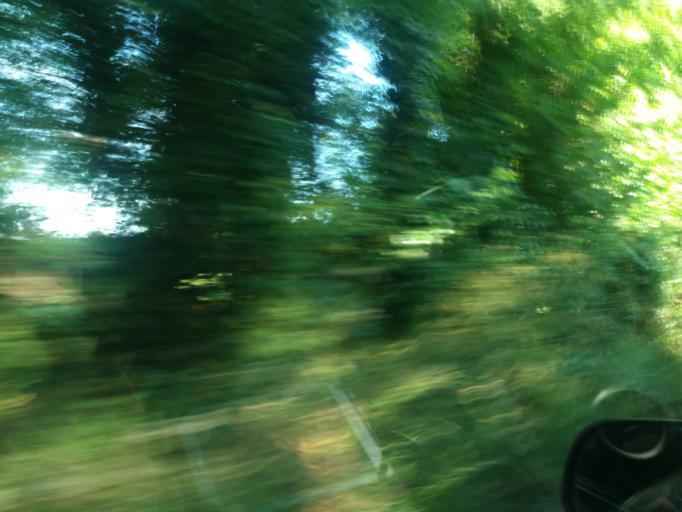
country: IE
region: Leinster
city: Hartstown
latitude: 53.3711
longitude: -6.4097
